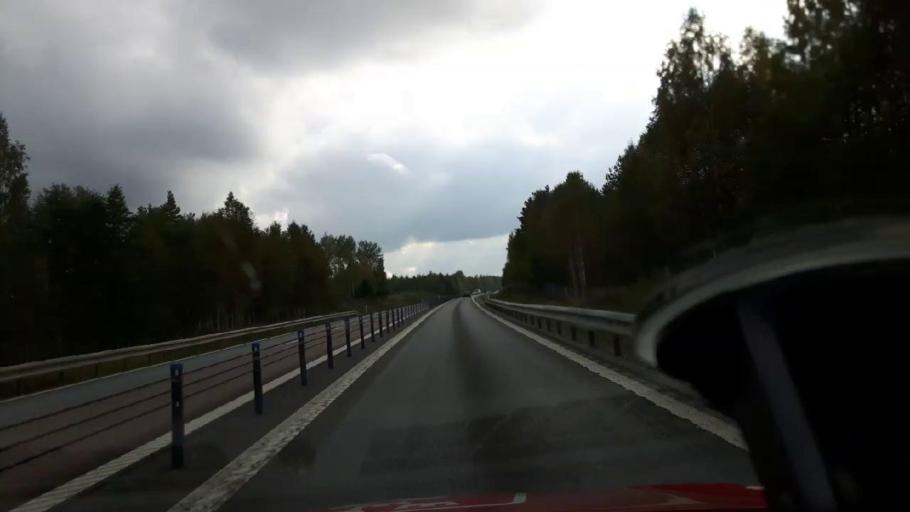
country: SE
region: Gaevleborg
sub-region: Gavle Kommun
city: Norrsundet
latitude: 60.8219
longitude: 17.0845
